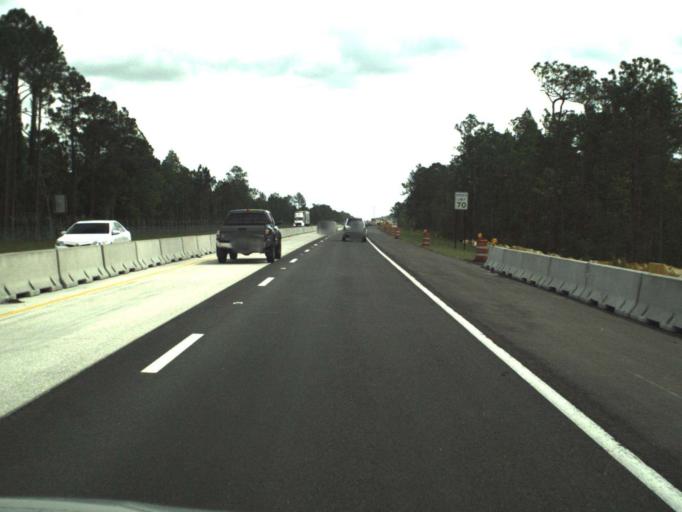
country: US
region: Florida
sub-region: Volusia County
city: Samsula-Spruce Creek
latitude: 29.0916
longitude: -81.1619
